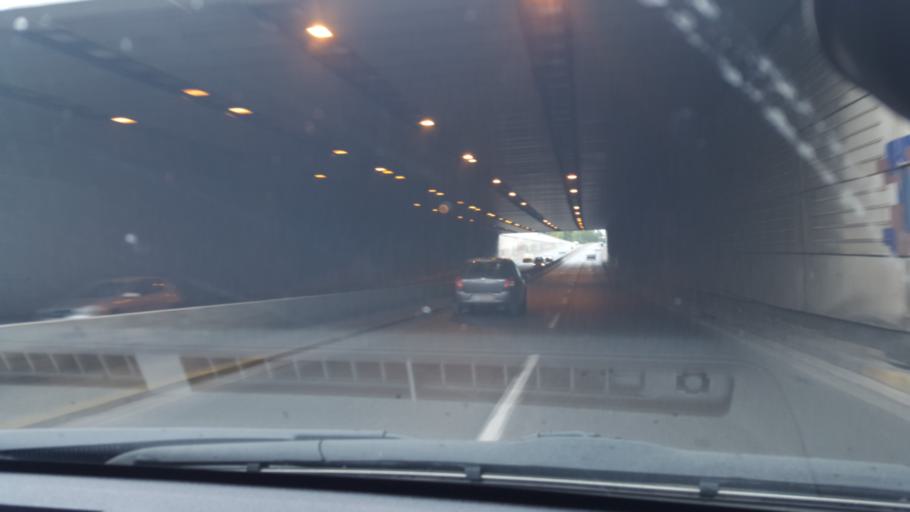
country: GR
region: Attica
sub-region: Nomarchia Athinas
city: Neo Psychiko
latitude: 38.0042
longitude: 23.7752
